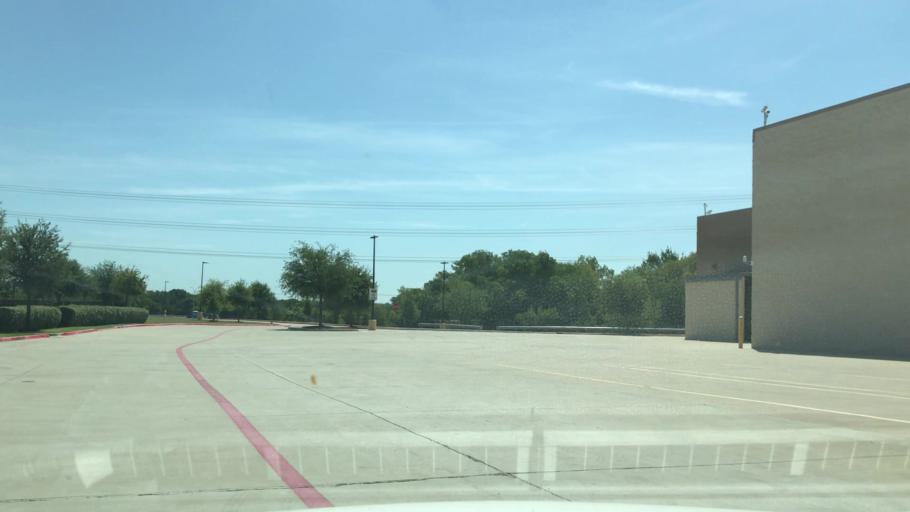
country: US
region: Texas
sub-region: Collin County
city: Allen
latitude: 33.1203
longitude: -96.6721
